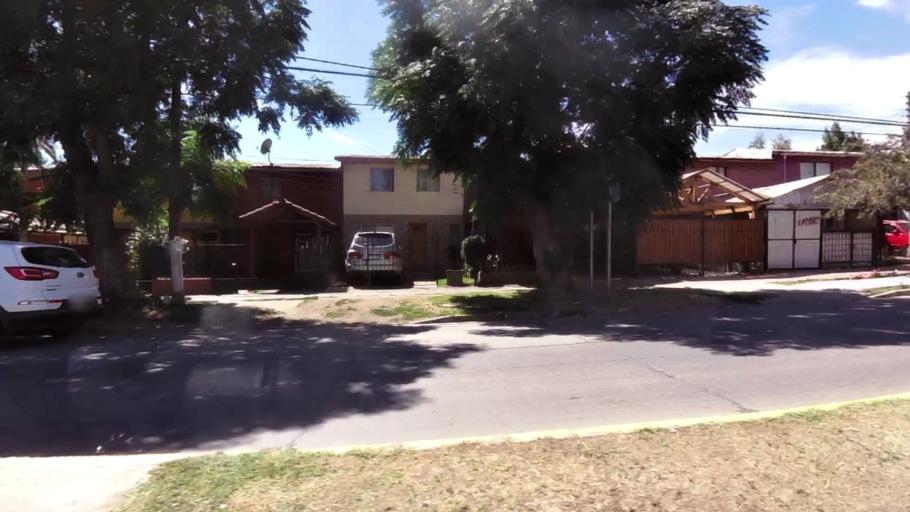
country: CL
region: O'Higgins
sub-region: Provincia de Cachapoal
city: Graneros
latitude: -33.9761
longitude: -70.7120
